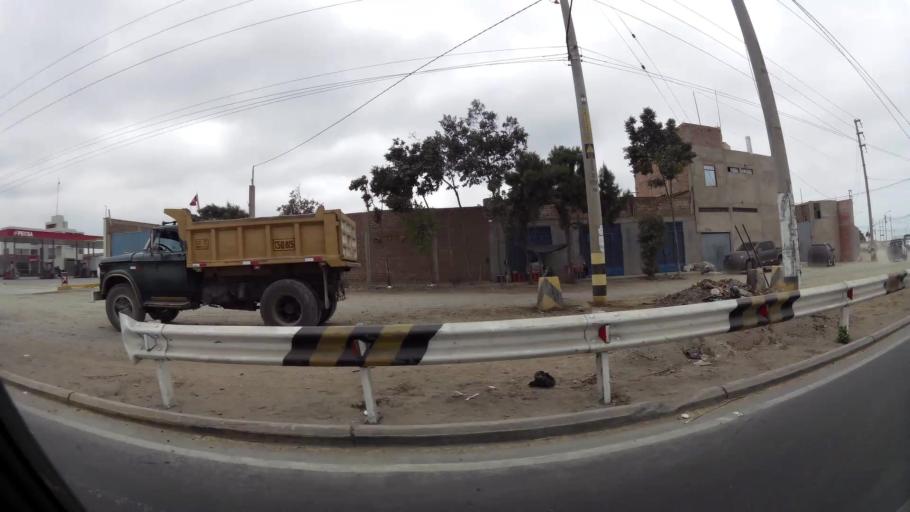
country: PE
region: La Libertad
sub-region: Provincia de Trujillo
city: Huanchaco
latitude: -8.0863
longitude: -79.0961
